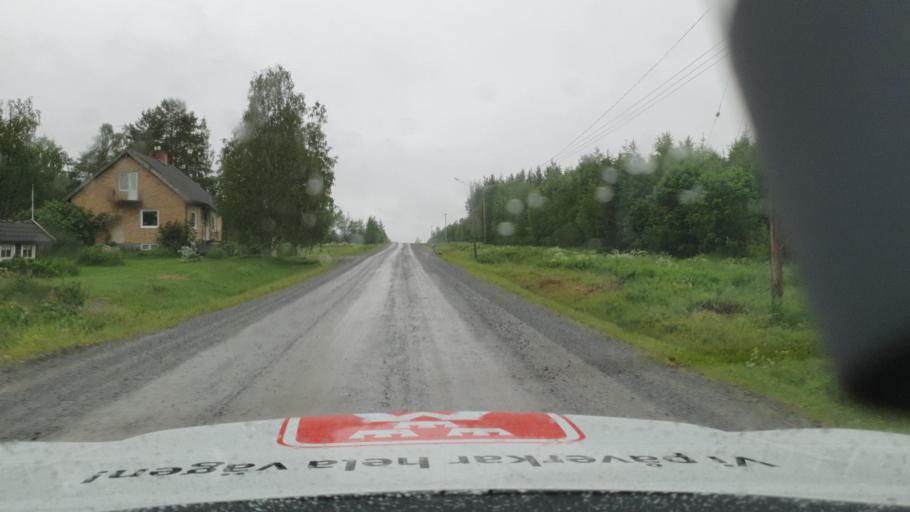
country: SE
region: Vaesterbotten
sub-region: Bjurholms Kommun
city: Bjurholm
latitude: 63.8730
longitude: 19.4533
